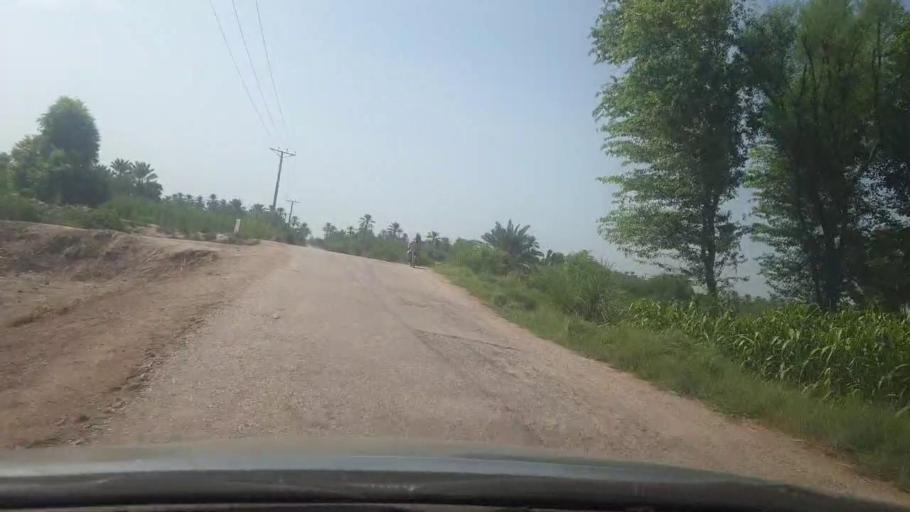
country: PK
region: Sindh
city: Gambat
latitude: 27.3283
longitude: 68.5508
